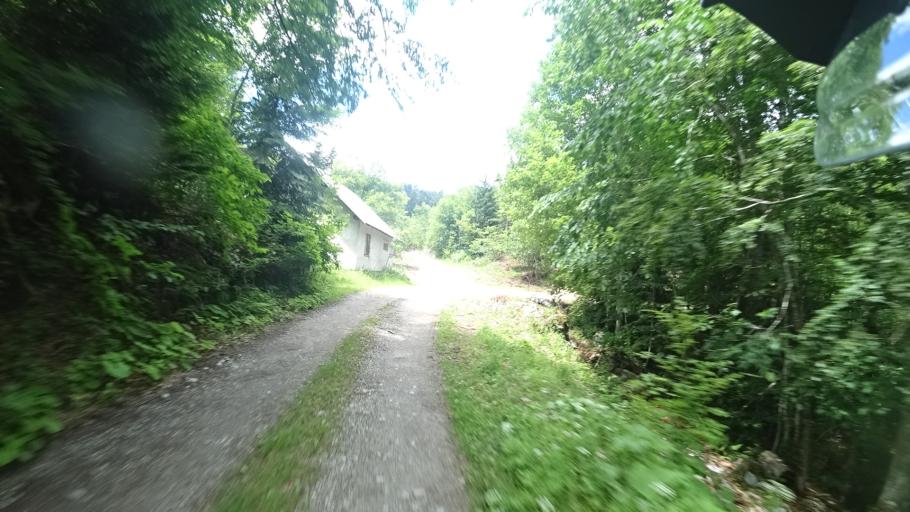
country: SI
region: Osilnica
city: Osilnica
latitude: 45.4942
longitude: 14.7334
